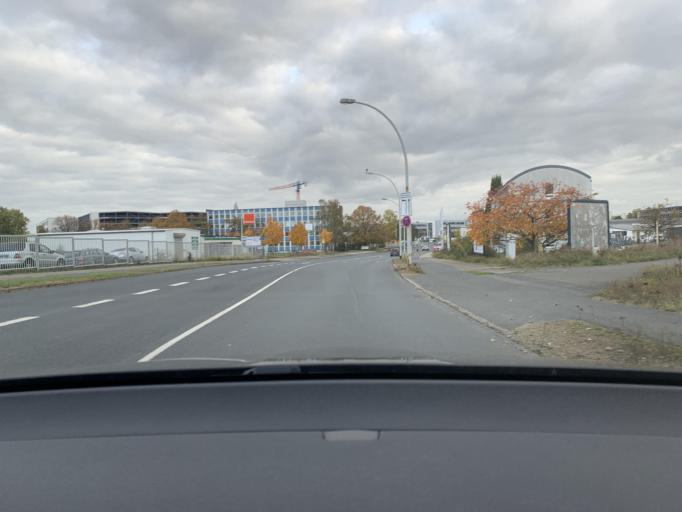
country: DE
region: Lower Saxony
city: Braunschweig
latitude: 52.2992
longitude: 10.5097
